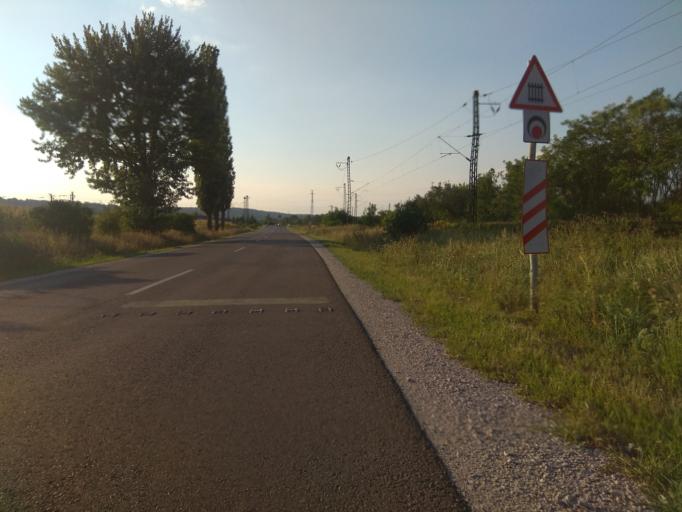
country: HU
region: Borsod-Abauj-Zemplen
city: Nyekladhaza
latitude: 47.9843
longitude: 20.8411
